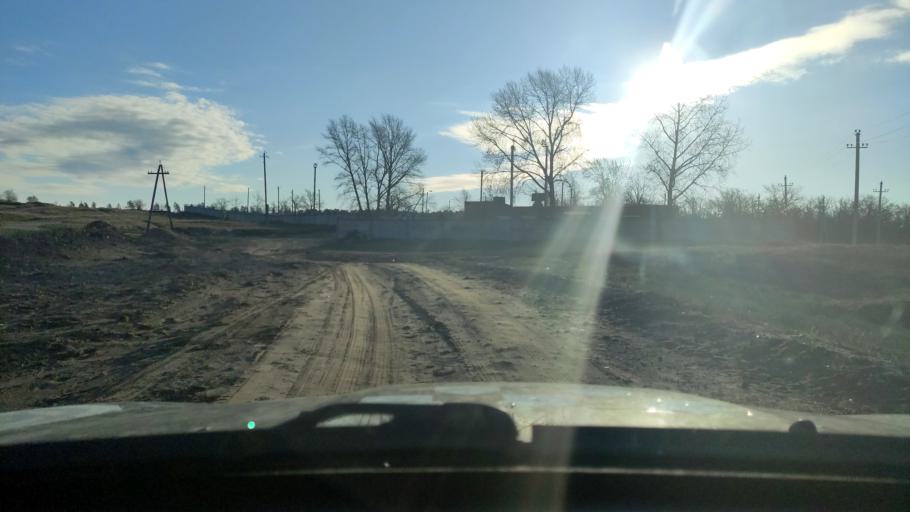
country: RU
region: Samara
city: Zhigulevsk
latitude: 53.4792
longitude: 49.5334
